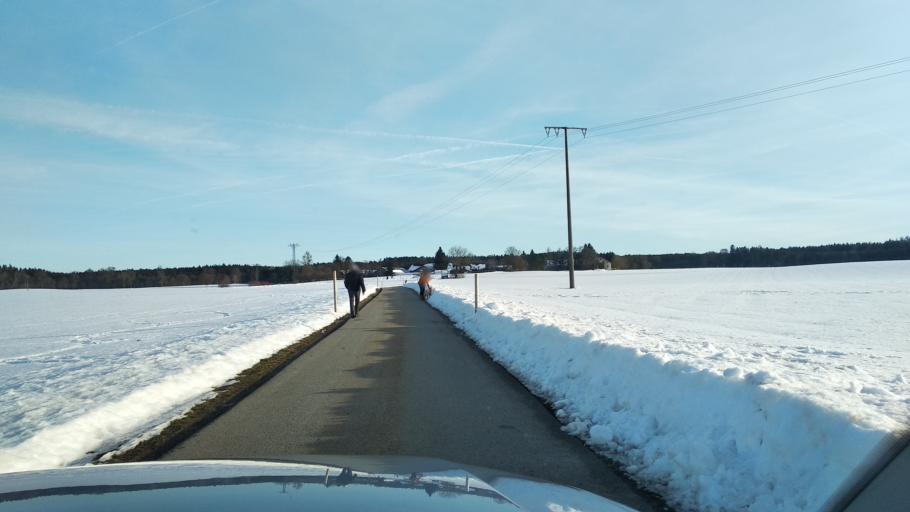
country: DE
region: Bavaria
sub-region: Upper Bavaria
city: Kirchseeon
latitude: 48.0744
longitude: 11.8649
